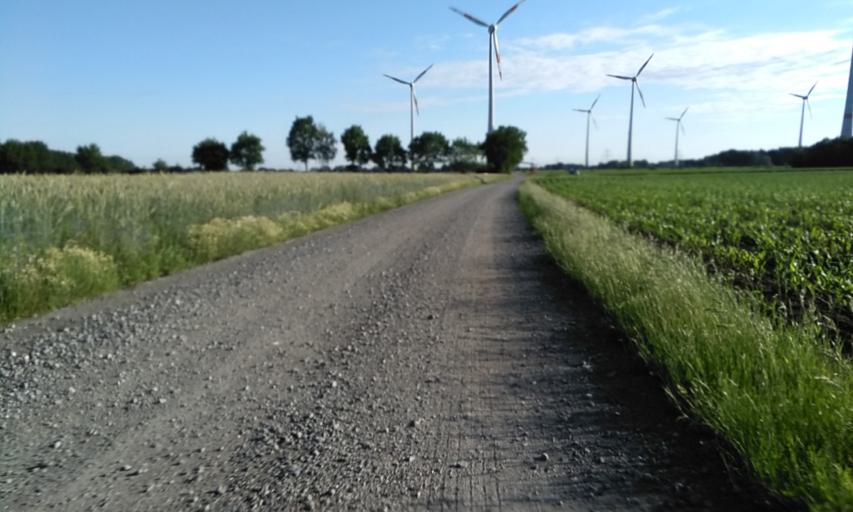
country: DE
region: Lower Saxony
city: Deinste
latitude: 53.5107
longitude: 9.4589
